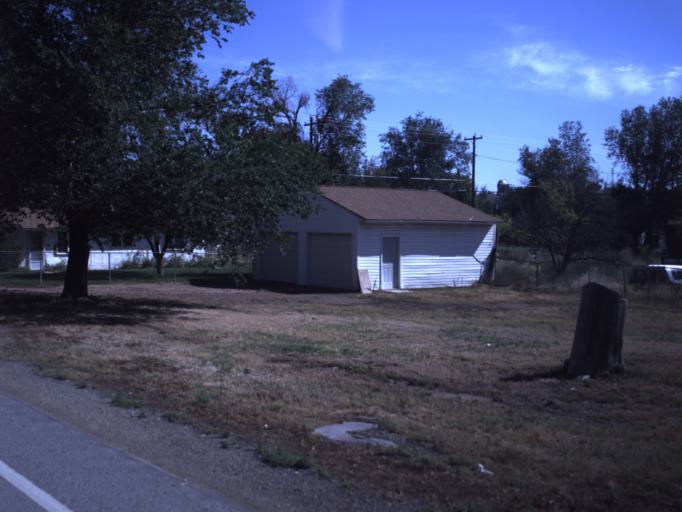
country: US
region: Utah
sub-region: Duchesne County
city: Duchesne
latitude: 40.1612
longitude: -110.4031
